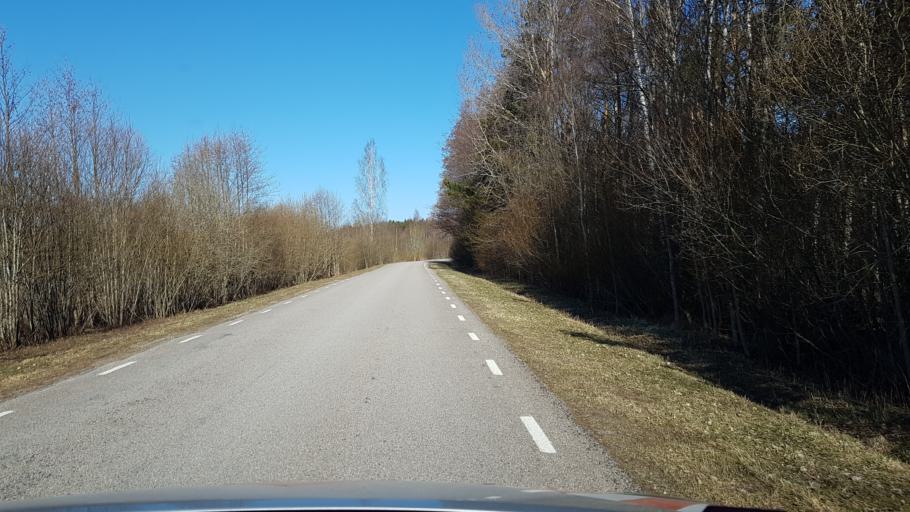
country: EE
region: Harju
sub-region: Loksa linn
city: Loksa
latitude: 59.5839
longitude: 25.9096
